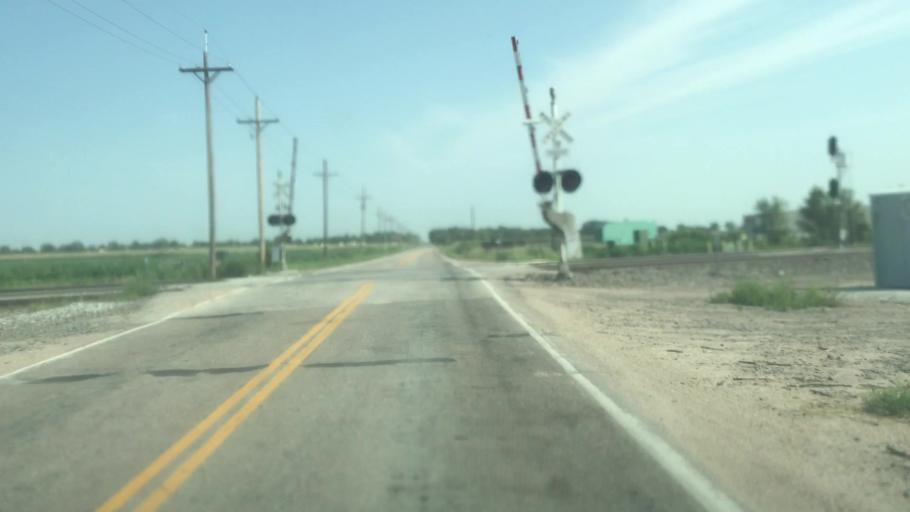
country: US
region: Nebraska
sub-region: Hall County
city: Grand Island
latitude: 40.9416
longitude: -98.3015
